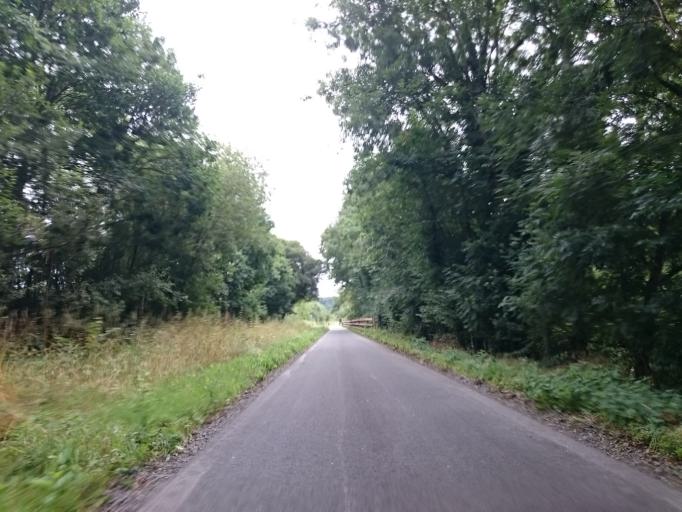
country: FR
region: Lower Normandy
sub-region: Departement du Calvados
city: Thury-Harcourt
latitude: 49.0180
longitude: -0.4670
